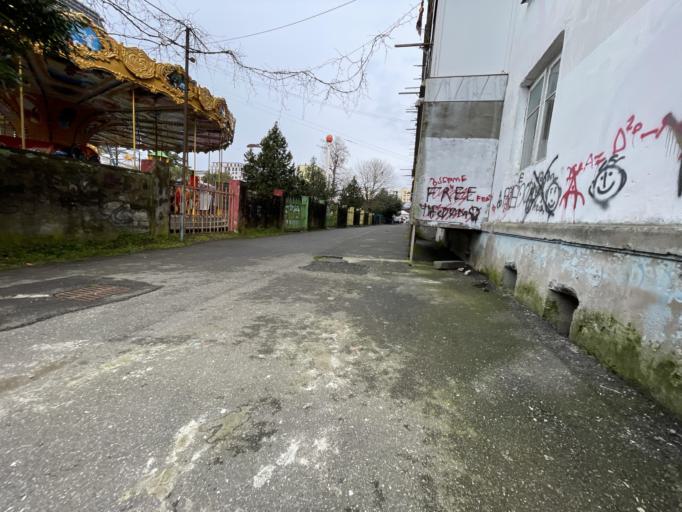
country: GE
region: Ajaria
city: Batumi
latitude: 41.6469
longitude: 41.6288
